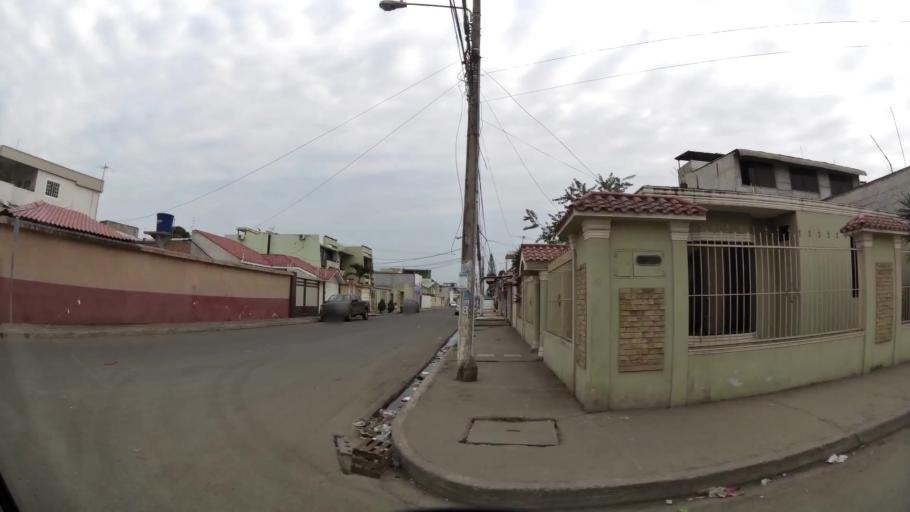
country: EC
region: El Oro
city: Machala
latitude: -3.2491
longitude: -79.9601
